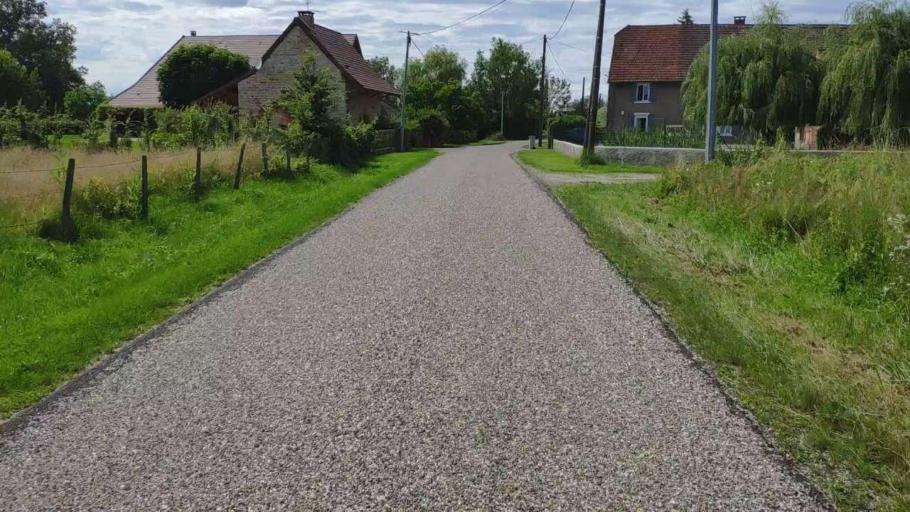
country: FR
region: Franche-Comte
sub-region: Departement du Jura
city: Bletterans
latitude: 46.8191
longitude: 5.4522
